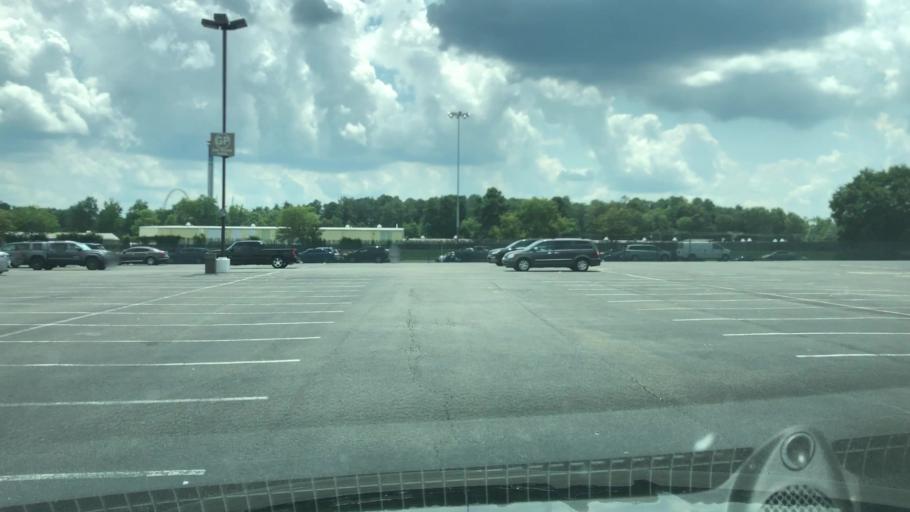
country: US
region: Virginia
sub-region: Hanover County
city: Ashland
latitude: 37.8428
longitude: -77.4479
